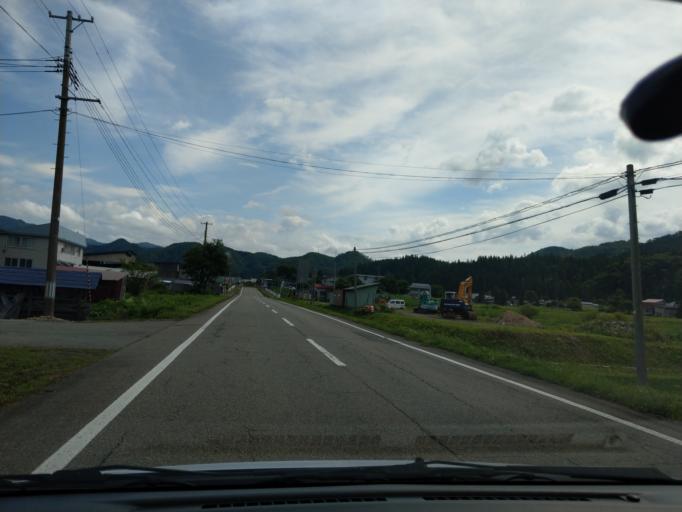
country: JP
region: Akita
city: Kakunodatemachi
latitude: 39.7389
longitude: 140.5856
